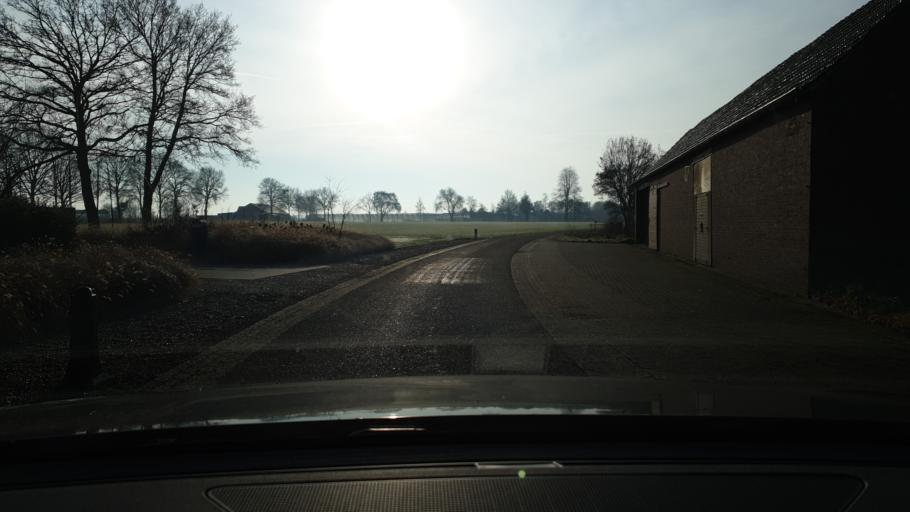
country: NL
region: Limburg
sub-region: Gemeente Peel en Maas
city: Maasbree
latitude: 51.4299
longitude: 6.0485
